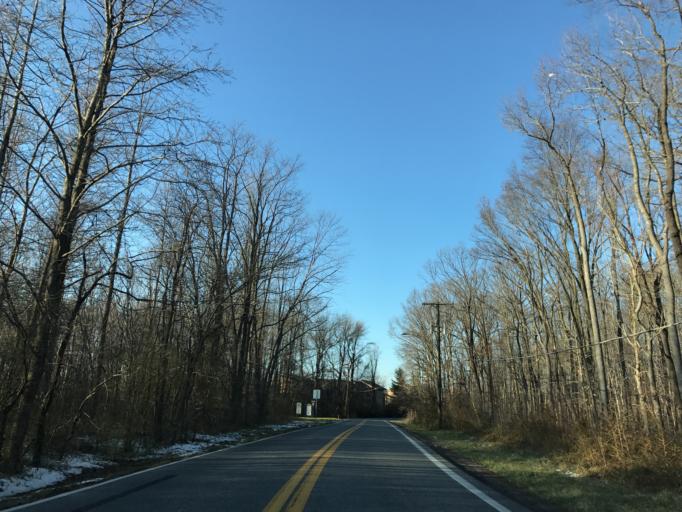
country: US
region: Maryland
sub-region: Baltimore County
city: Essex
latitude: 39.2961
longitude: -76.4412
